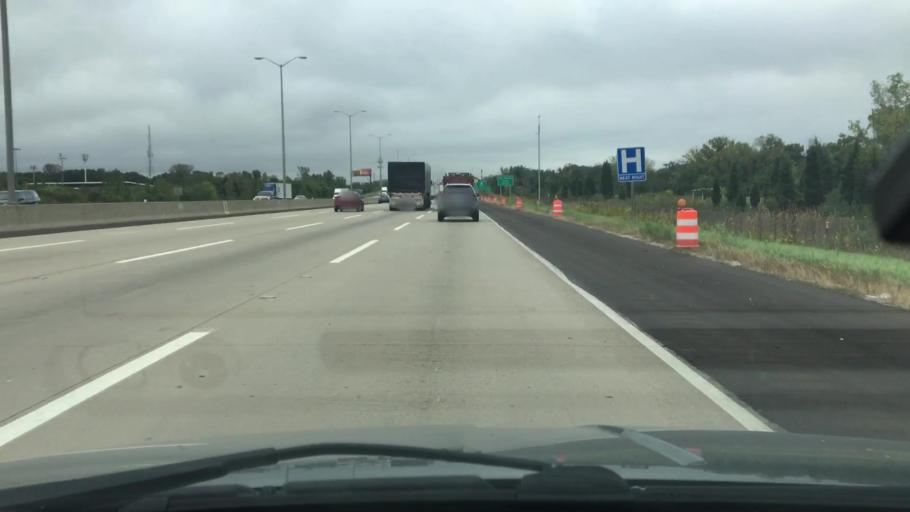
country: US
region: Illinois
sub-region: Cook County
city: Des Plaines
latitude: 42.0715
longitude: -87.8671
